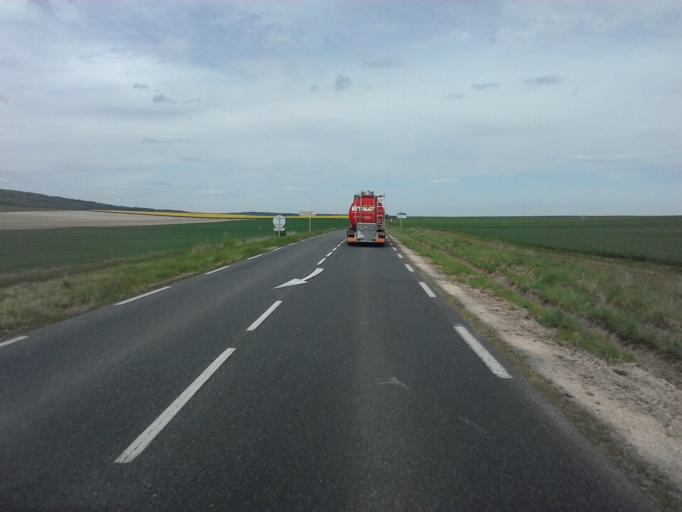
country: FR
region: Bourgogne
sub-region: Departement de l'Yonne
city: Neuvy-Sautour
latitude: 48.0672
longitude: 3.8120
